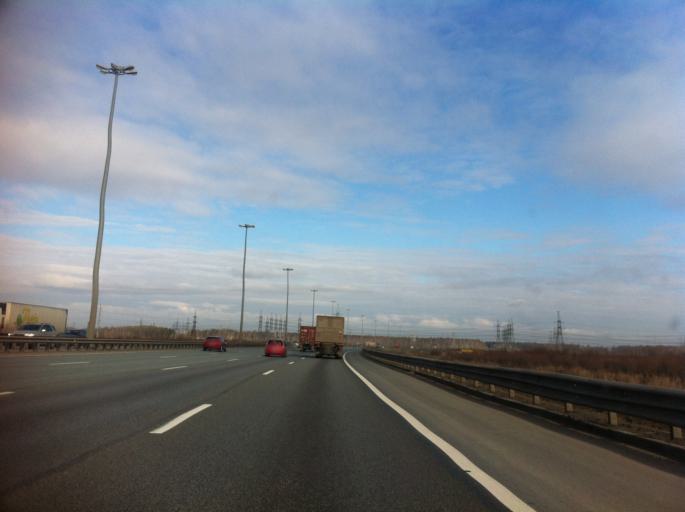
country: RU
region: St.-Petersburg
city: Krasnogvargeisky
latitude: 59.9176
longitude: 30.5261
